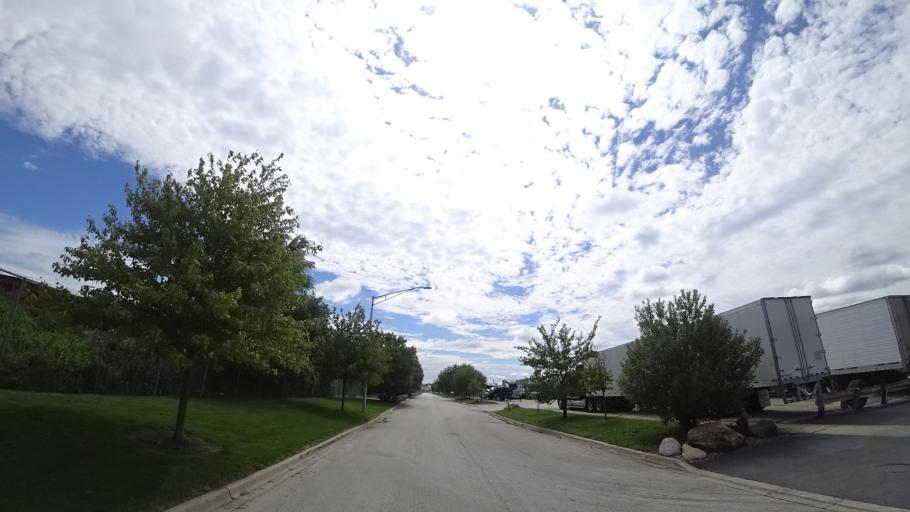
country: US
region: Illinois
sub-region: Cook County
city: Chicago Ridge
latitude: 41.7103
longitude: -87.7892
